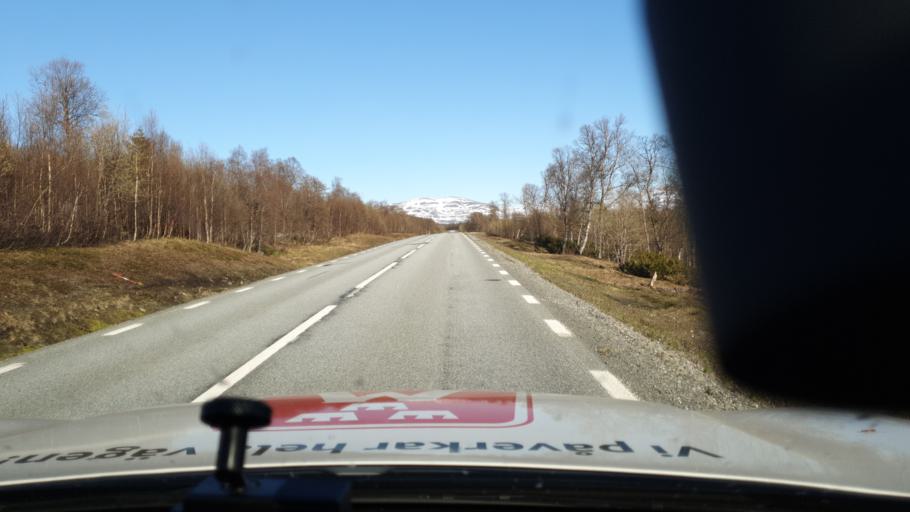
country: NO
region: Nordland
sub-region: Rana
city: Mo i Rana
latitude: 66.0522
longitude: 14.9287
